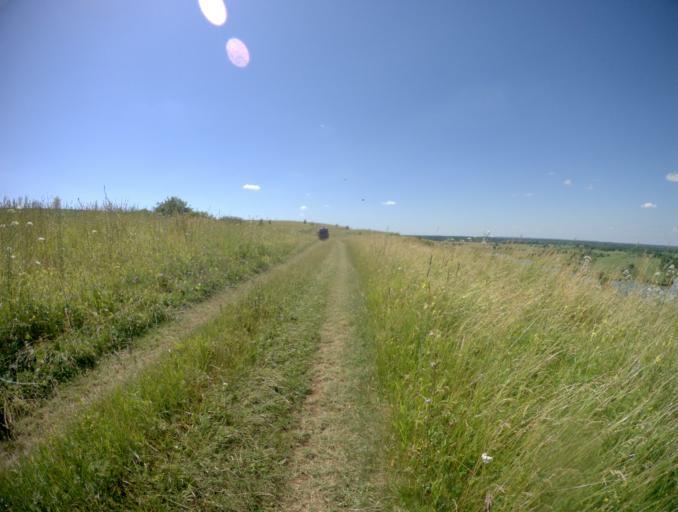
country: RU
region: Nizjnij Novgorod
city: Gorbatov
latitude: 56.1377
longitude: 43.0146
